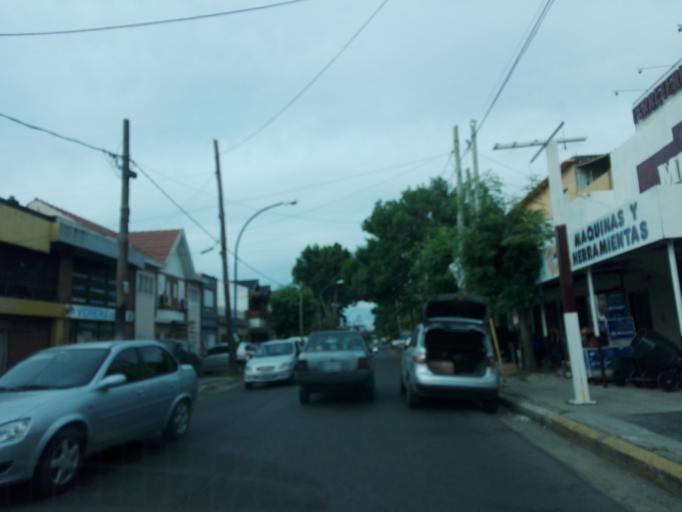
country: AR
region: Buenos Aires
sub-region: Partido de Lanus
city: Lanus
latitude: -34.7112
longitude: -58.3769
